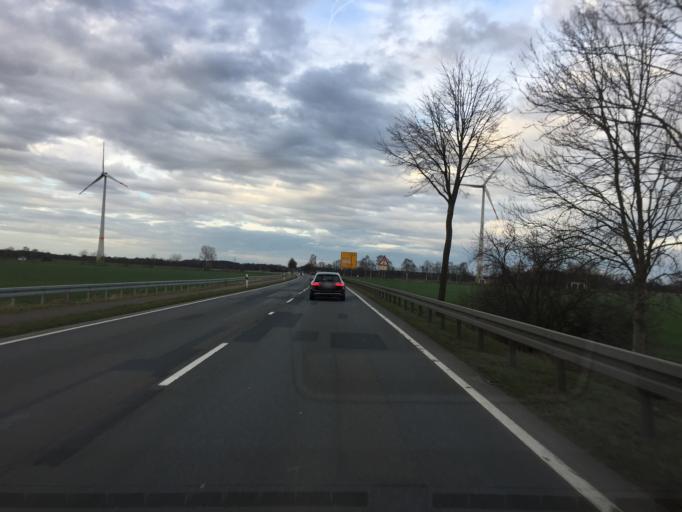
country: DE
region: Lower Saxony
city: Barenburg
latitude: 52.6356
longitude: 8.8051
